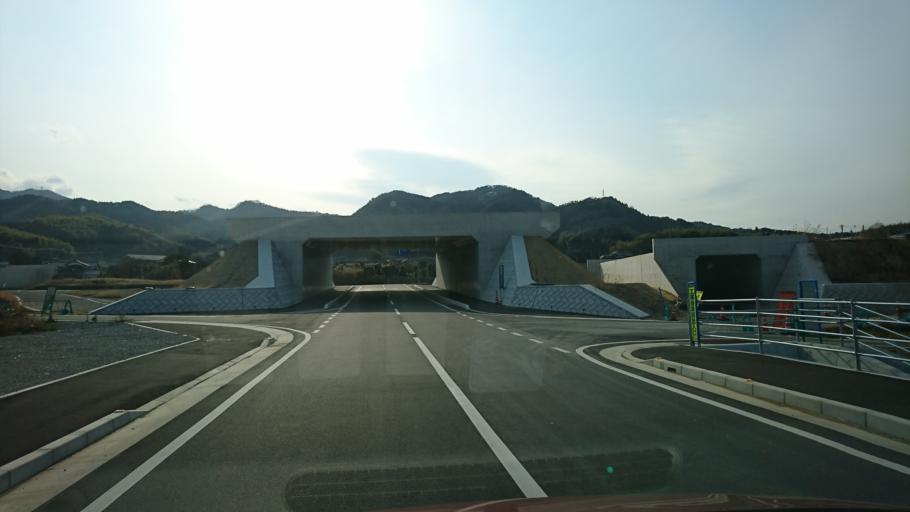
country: JP
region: Ehime
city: Hojo
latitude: 34.0199
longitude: 132.9903
